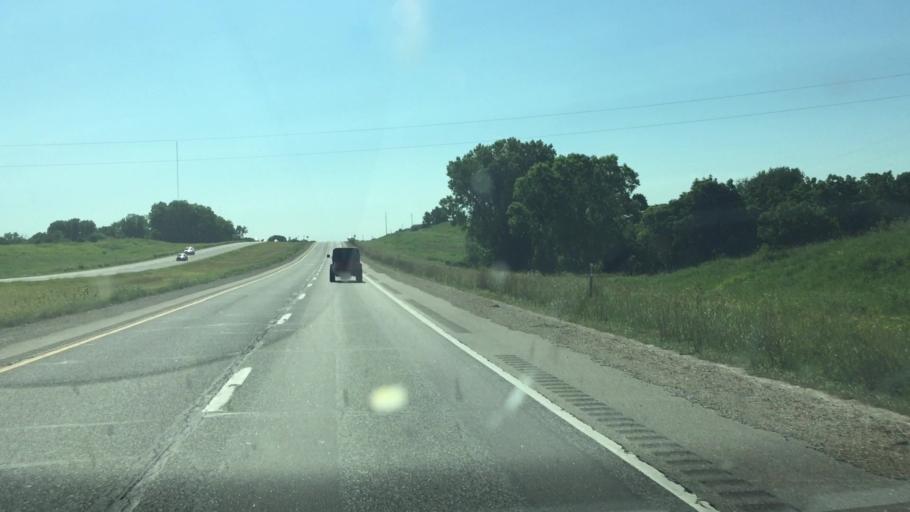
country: US
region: Iowa
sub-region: Linn County
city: Ely
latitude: 41.9261
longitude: -91.5984
